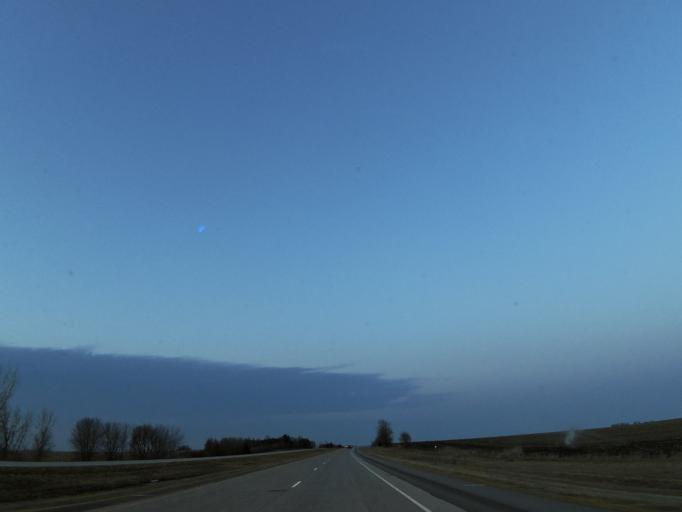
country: US
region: Minnesota
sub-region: Mower County
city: Grand Meadow
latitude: 43.7801
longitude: -92.6199
